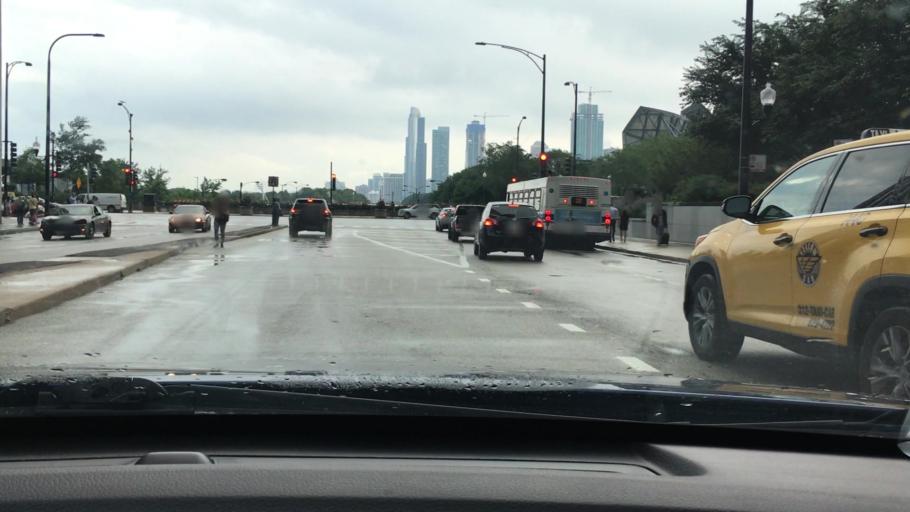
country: US
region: Illinois
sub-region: Cook County
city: Chicago
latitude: 41.8854
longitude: -87.6207
